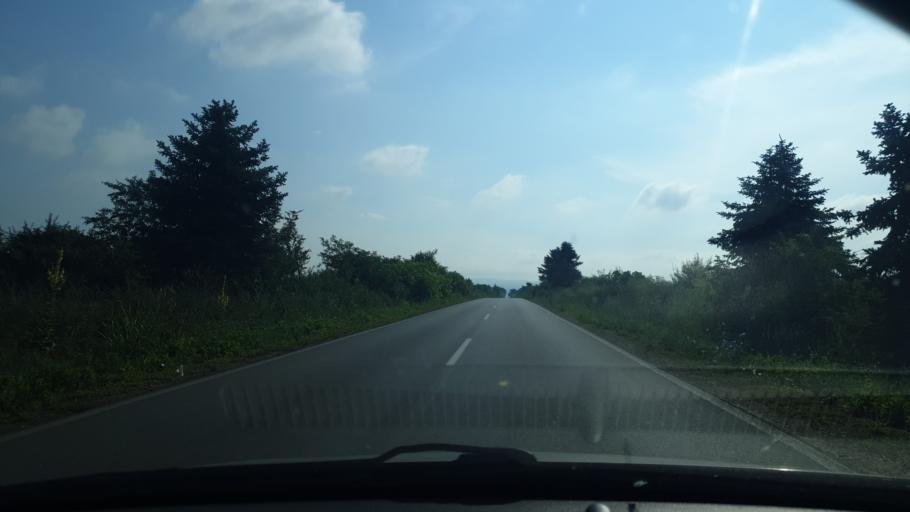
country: RS
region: Central Serbia
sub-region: Pomoravski Okrug
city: Cuprija
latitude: 43.9370
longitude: 21.3949
